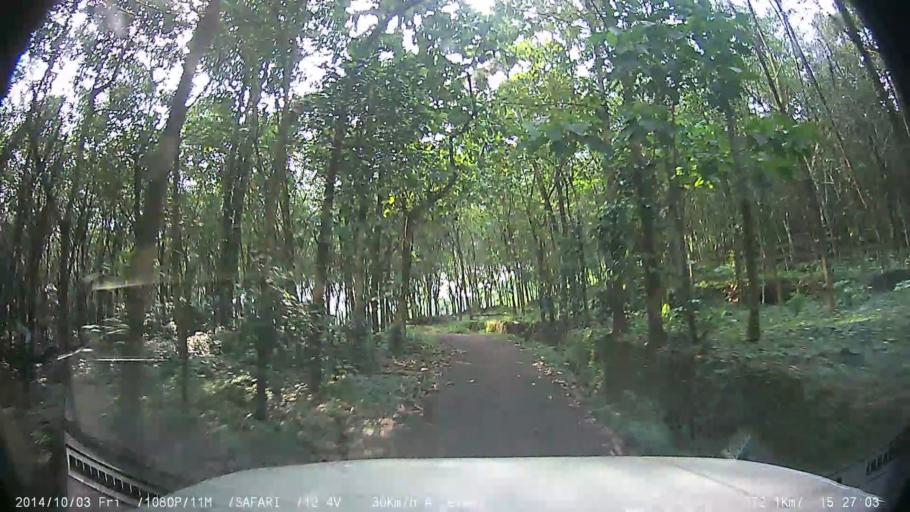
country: IN
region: Kerala
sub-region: Ernakulam
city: Muvattupuzha
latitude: 9.9284
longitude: 76.5721
